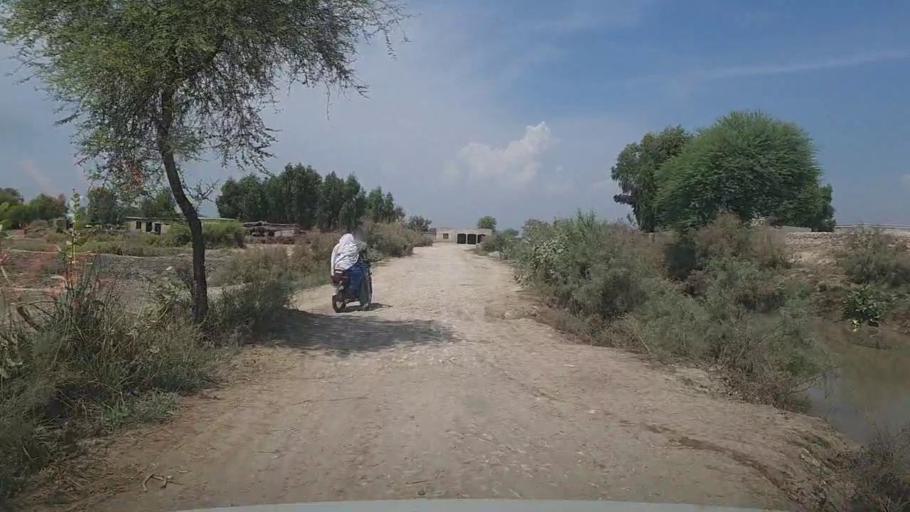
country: PK
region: Sindh
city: Kandhkot
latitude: 28.2784
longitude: 69.2345
